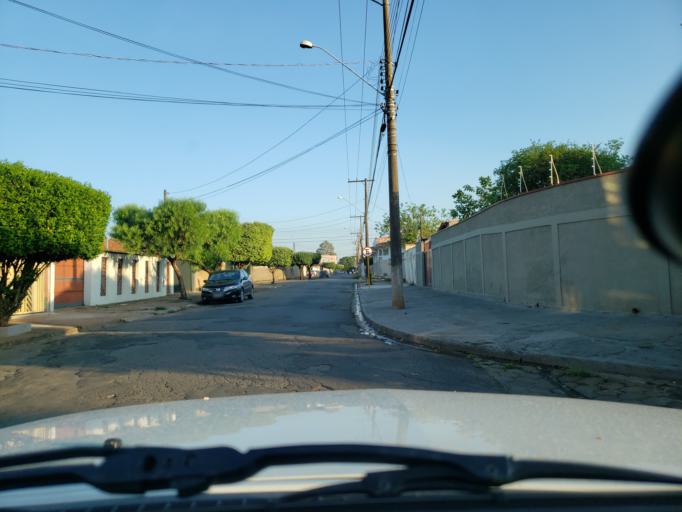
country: BR
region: Sao Paulo
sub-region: Moji-Guacu
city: Mogi-Gaucu
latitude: -22.3430
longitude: -46.9387
